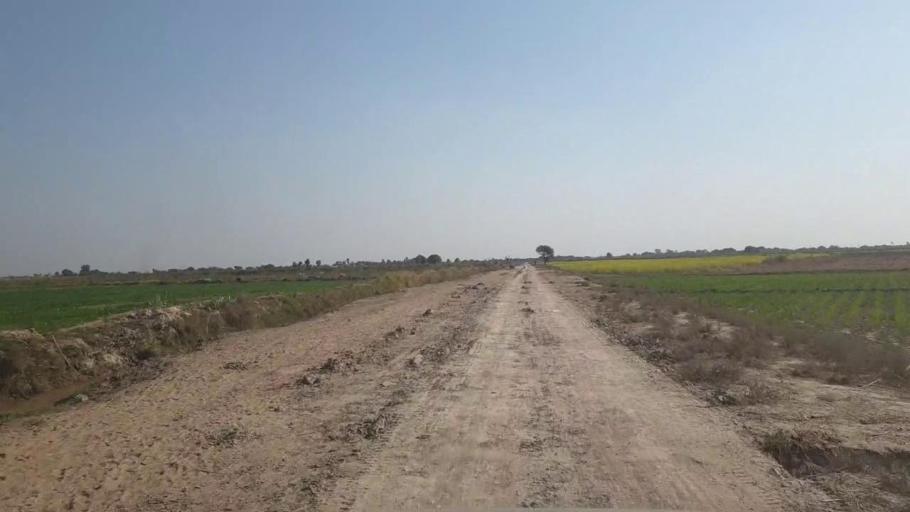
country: PK
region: Sindh
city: Chambar
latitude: 25.3196
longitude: 68.8704
